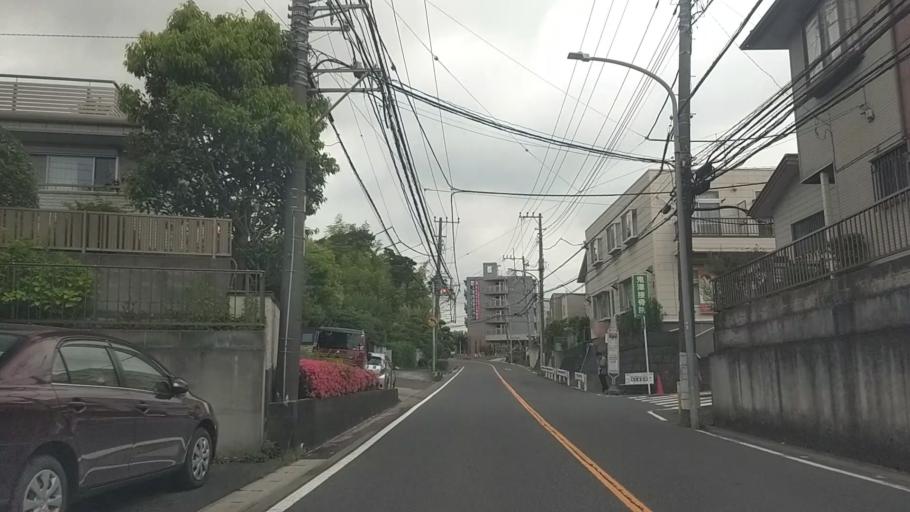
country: JP
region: Kanagawa
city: Kamakura
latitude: 35.3752
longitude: 139.5404
